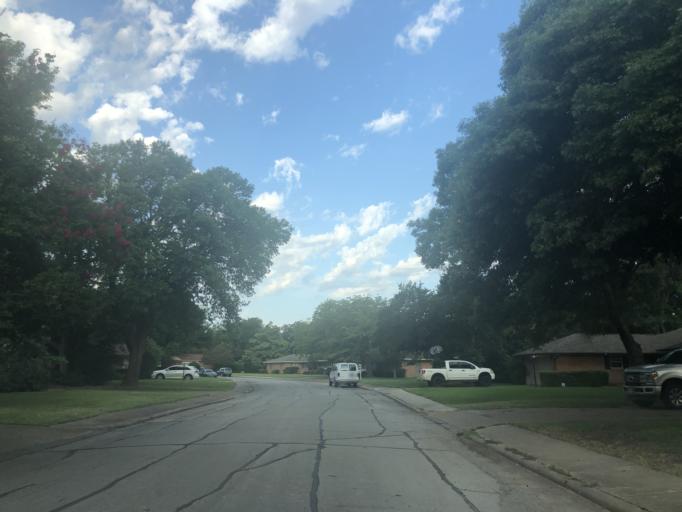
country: US
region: Texas
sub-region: Dallas County
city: Grand Prairie
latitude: 32.7626
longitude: -97.0150
